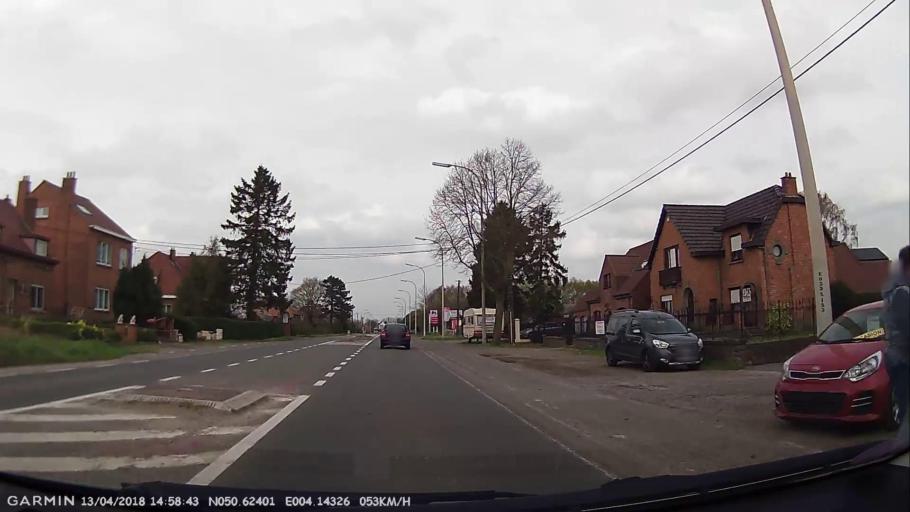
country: BE
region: Wallonia
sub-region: Province du Hainaut
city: Braine-le-Comte
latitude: 50.6241
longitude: 4.1433
